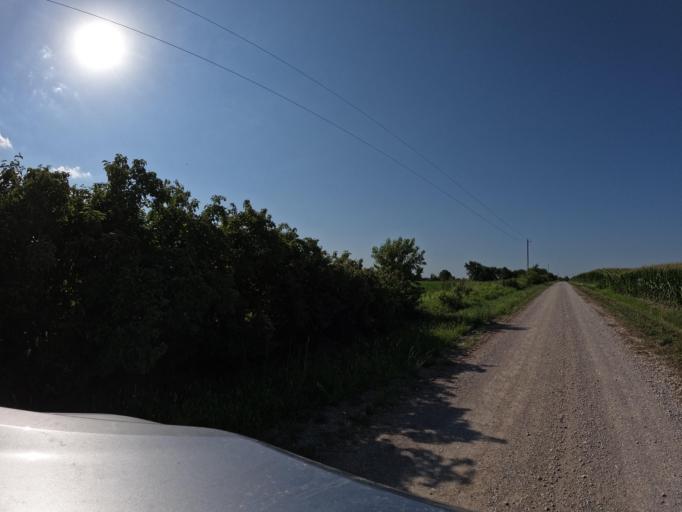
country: US
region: Iowa
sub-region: Appanoose County
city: Centerville
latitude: 40.7199
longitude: -93.0159
